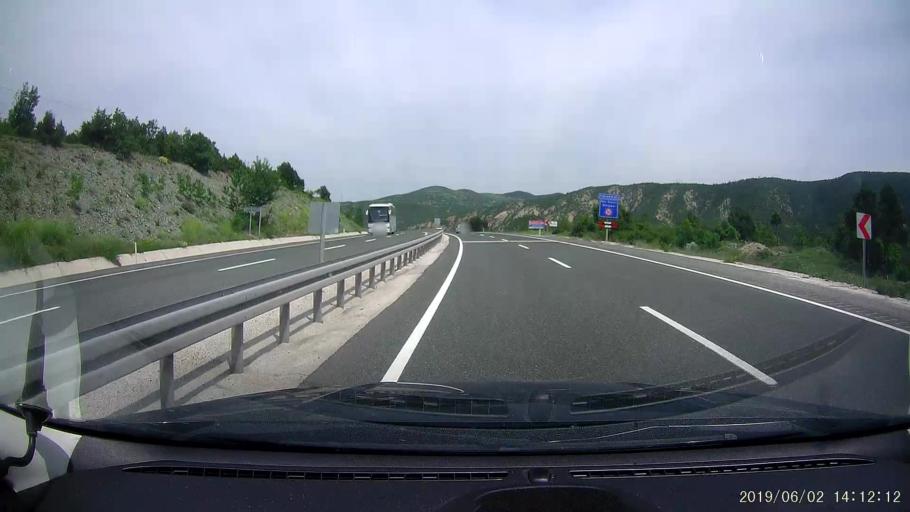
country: TR
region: Cankiri
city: Yaprakli
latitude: 40.9110
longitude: 33.8041
